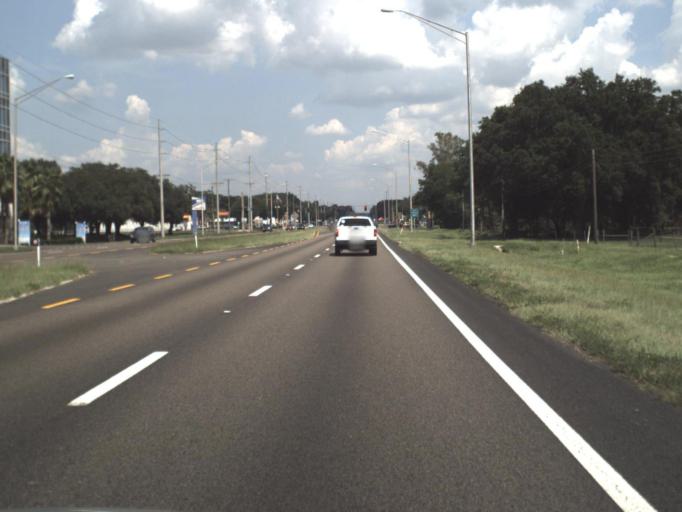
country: US
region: Florida
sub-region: Hillsborough County
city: Valrico
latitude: 27.9378
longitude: -82.2474
